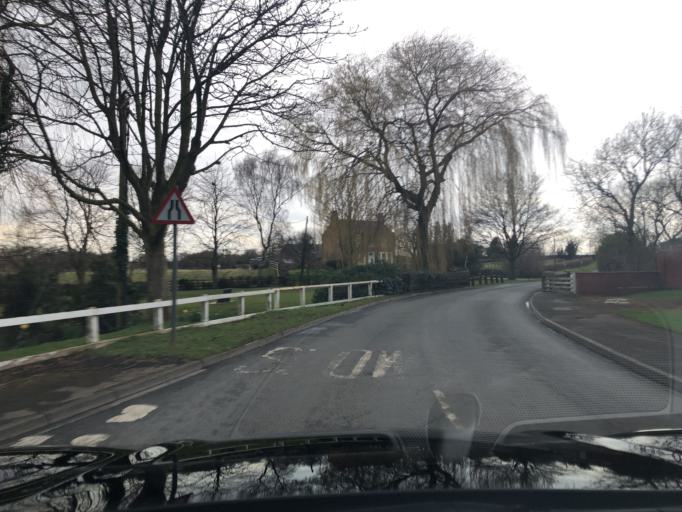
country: GB
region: England
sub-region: North Yorkshire
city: Northallerton
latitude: 54.3360
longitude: -1.4501
